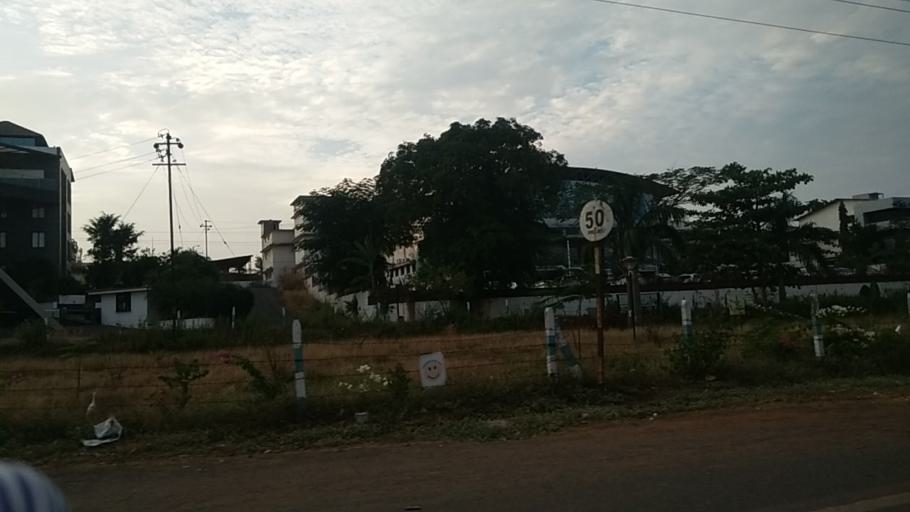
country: IN
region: Goa
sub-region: South Goa
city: Sancoale
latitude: 15.3651
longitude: 73.9261
